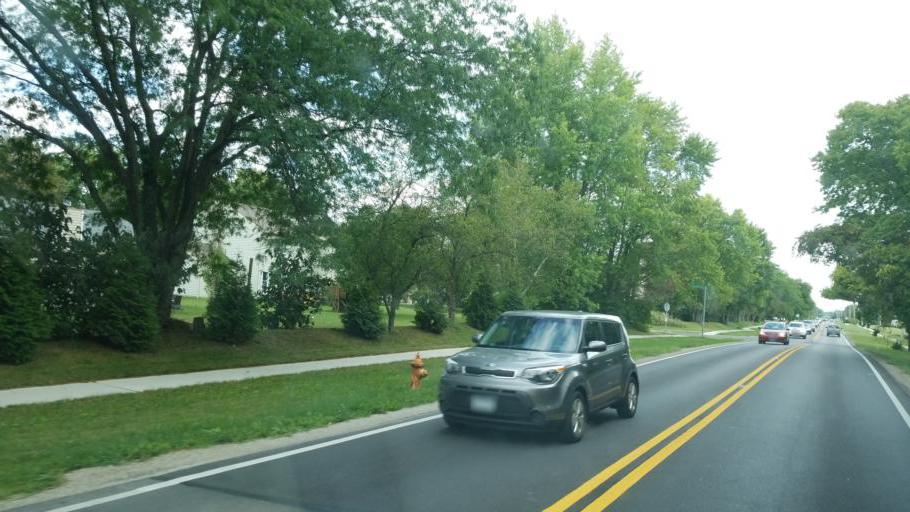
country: US
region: Ohio
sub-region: Delaware County
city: Powell
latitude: 40.1248
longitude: -83.0690
